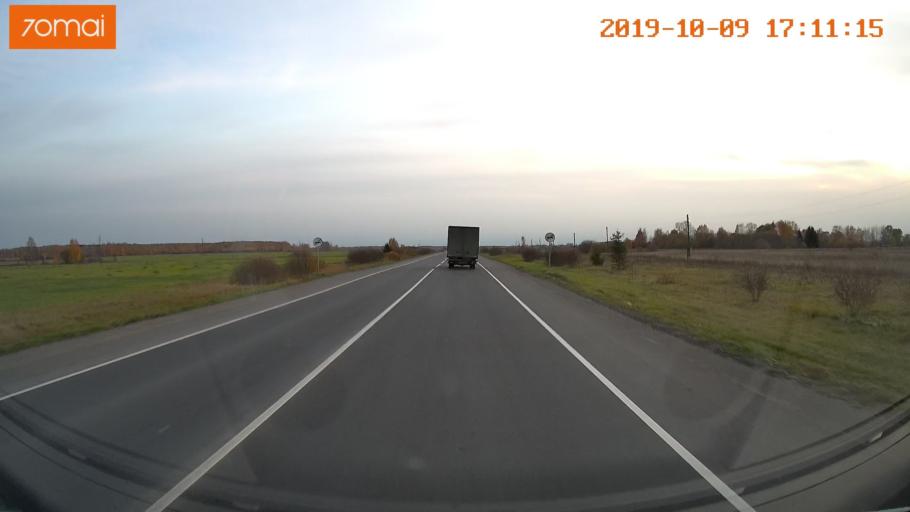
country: RU
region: Ivanovo
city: Privolzhsk
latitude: 57.3455
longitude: 41.2514
